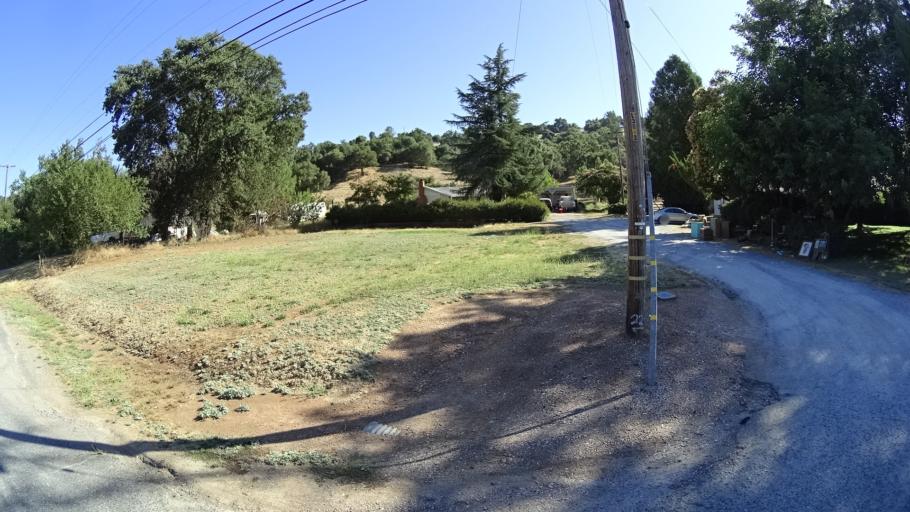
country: US
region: California
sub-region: Calaveras County
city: San Andreas
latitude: 38.2312
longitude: -120.7079
